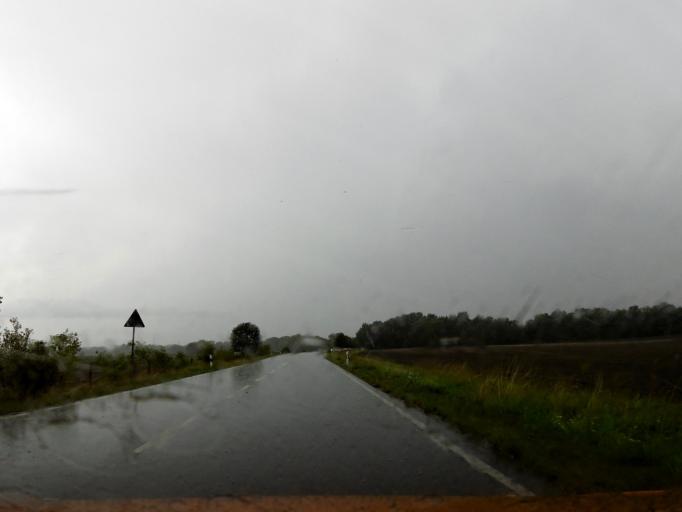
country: DE
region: Brandenburg
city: Werder
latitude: 52.4417
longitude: 12.9869
